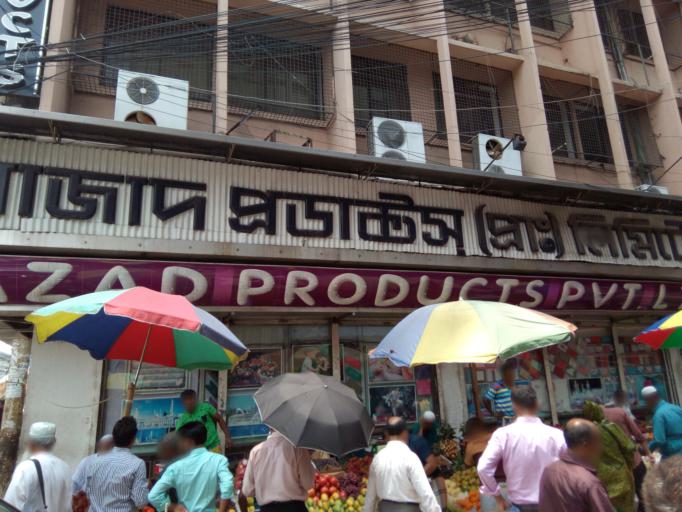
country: BD
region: Dhaka
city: Paltan
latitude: 23.7303
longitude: 90.4117
